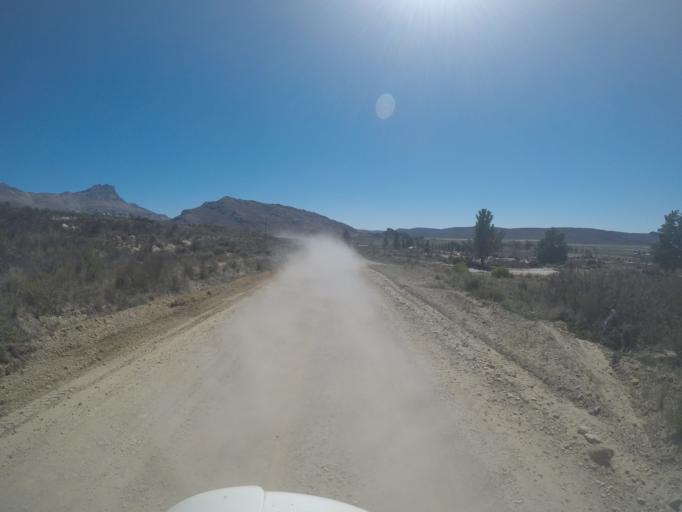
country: ZA
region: Western Cape
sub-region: Cape Winelands District Municipality
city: Ceres
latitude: -32.8696
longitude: 19.4438
